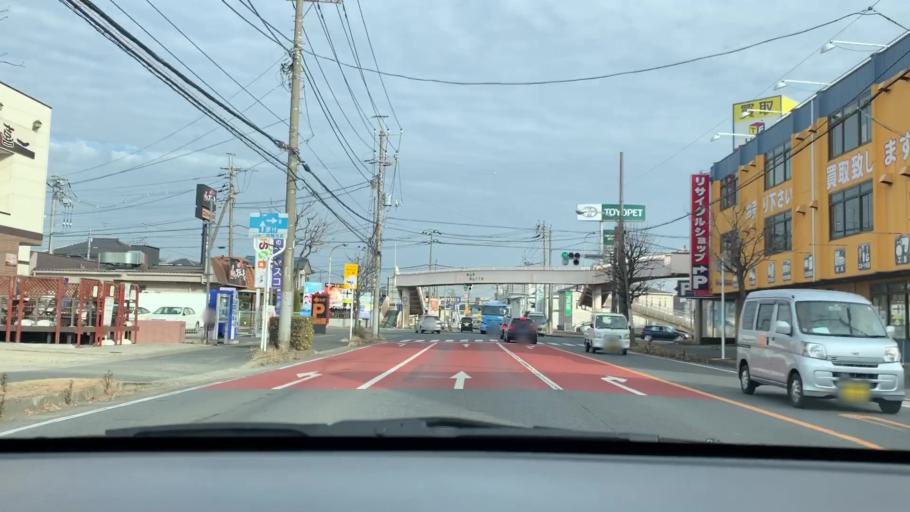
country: JP
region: Chiba
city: Nagareyama
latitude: 35.8439
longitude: 139.8977
